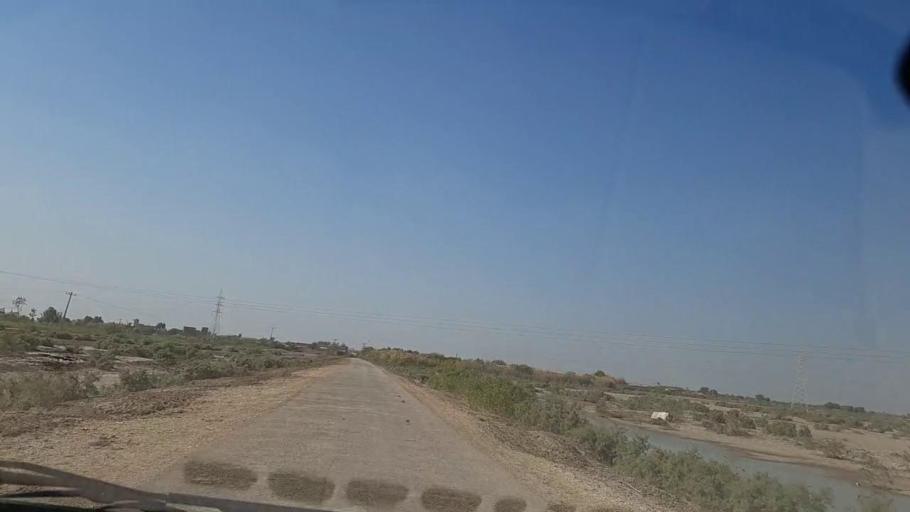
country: PK
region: Sindh
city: Mirpur Khas
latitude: 25.5214
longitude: 68.9466
